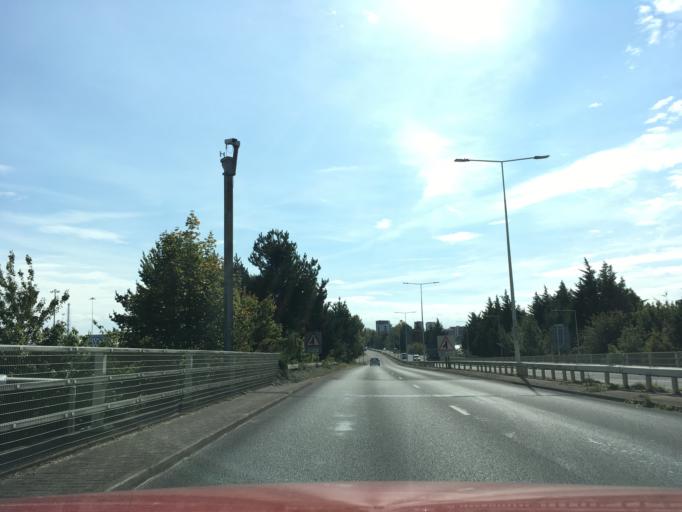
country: GB
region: Wales
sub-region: Cardiff
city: Cardiff
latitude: 51.4770
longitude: -3.1647
